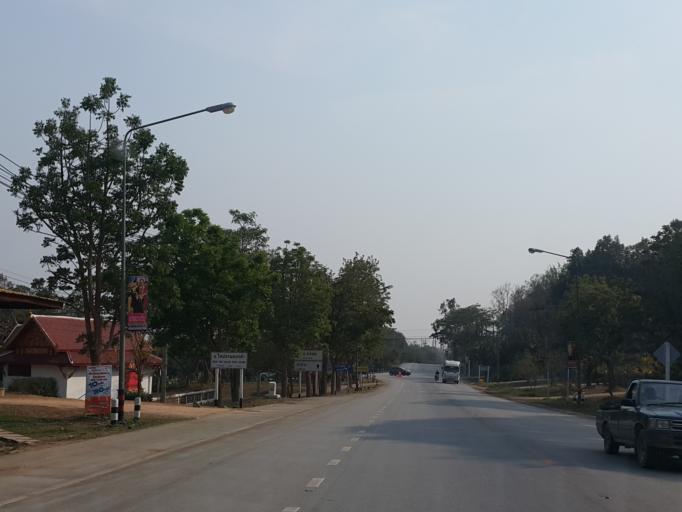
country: TH
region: Lampang
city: Chae Hom
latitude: 18.7070
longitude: 99.5552
